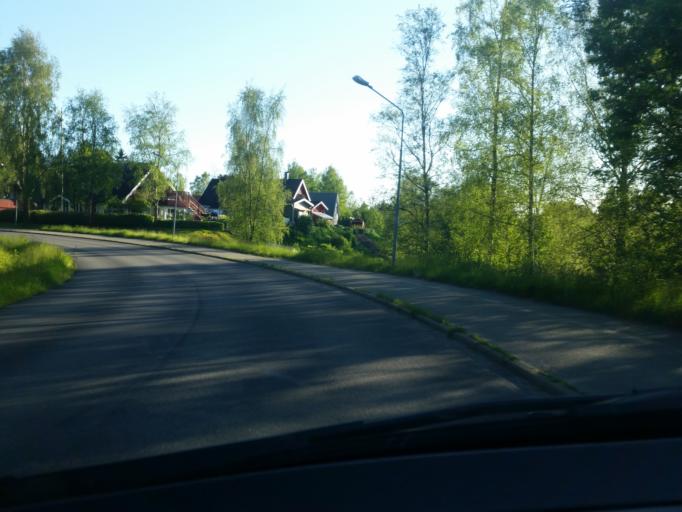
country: SE
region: Vaestra Goetaland
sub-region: Fargelanda Kommun
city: Faergelanda
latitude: 58.5617
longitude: 11.9892
